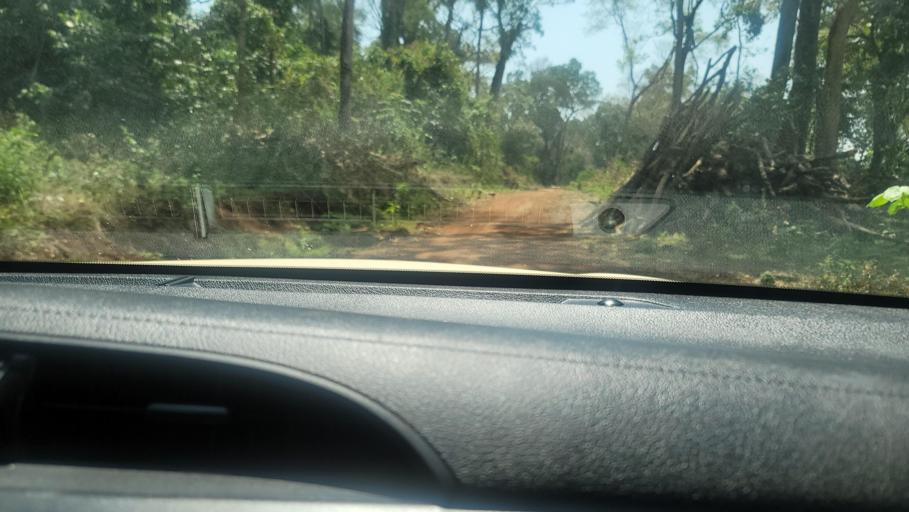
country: ET
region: Southern Nations, Nationalities, and People's Region
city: Bonga
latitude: 7.5436
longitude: 36.1793
